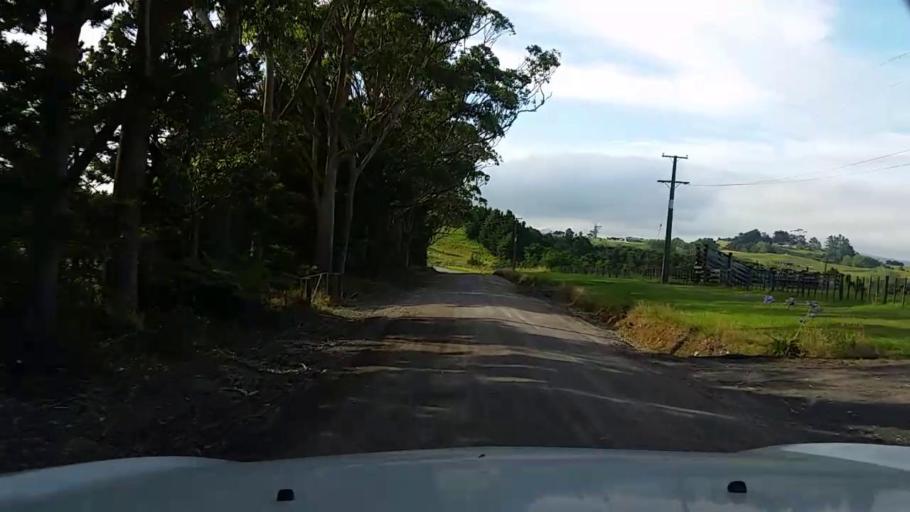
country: NZ
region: Northland
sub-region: Whangarei
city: Maungatapere
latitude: -35.6713
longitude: 174.1750
